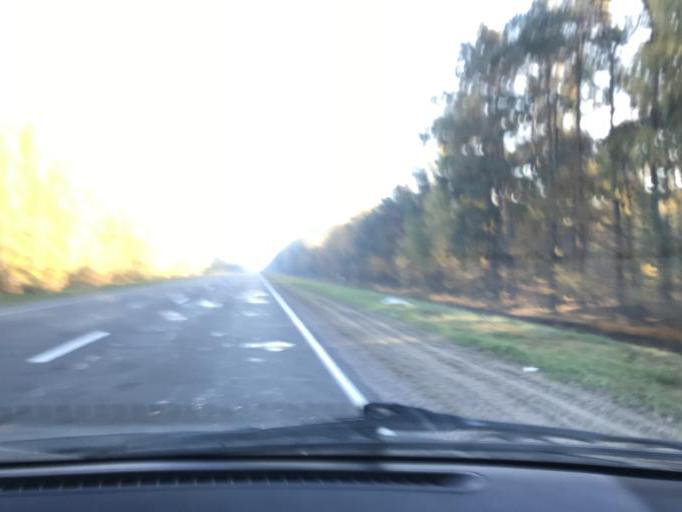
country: BY
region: Brest
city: Asnyezhytsy
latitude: 52.2360
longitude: 26.1817
